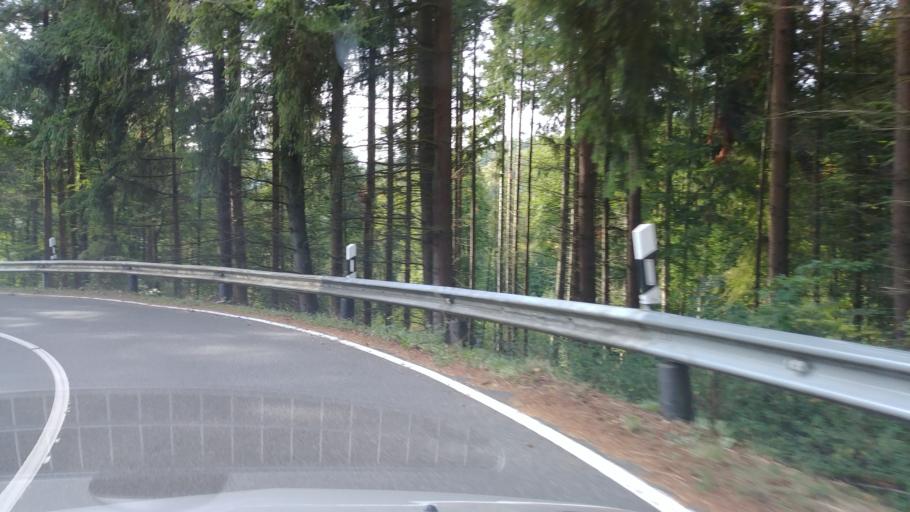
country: DE
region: Rheinland-Pfalz
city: Reckenroth
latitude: 50.2246
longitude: 8.0328
